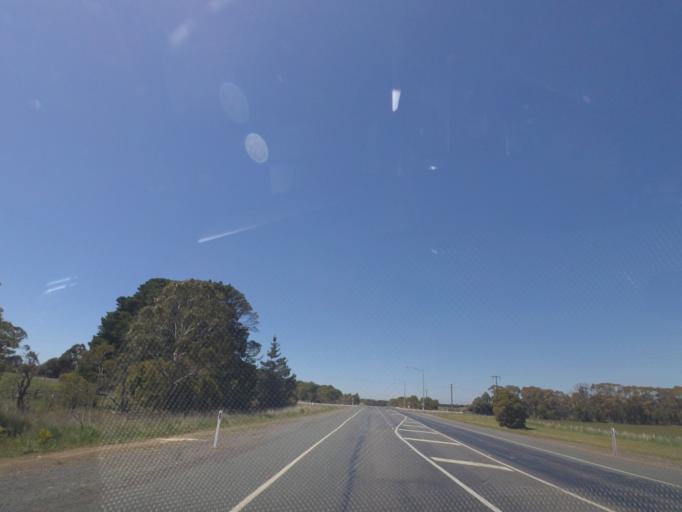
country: AU
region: Victoria
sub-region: Hume
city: Sunbury
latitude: -37.4256
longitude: 144.7271
